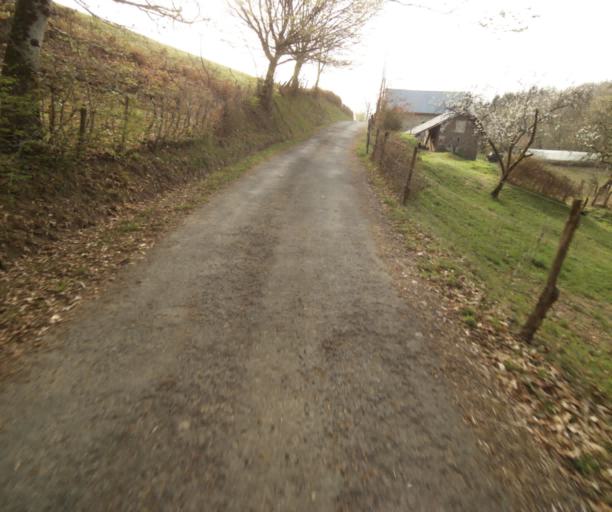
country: FR
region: Limousin
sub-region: Departement de la Correze
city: Chamboulive
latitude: 45.4318
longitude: 1.7912
